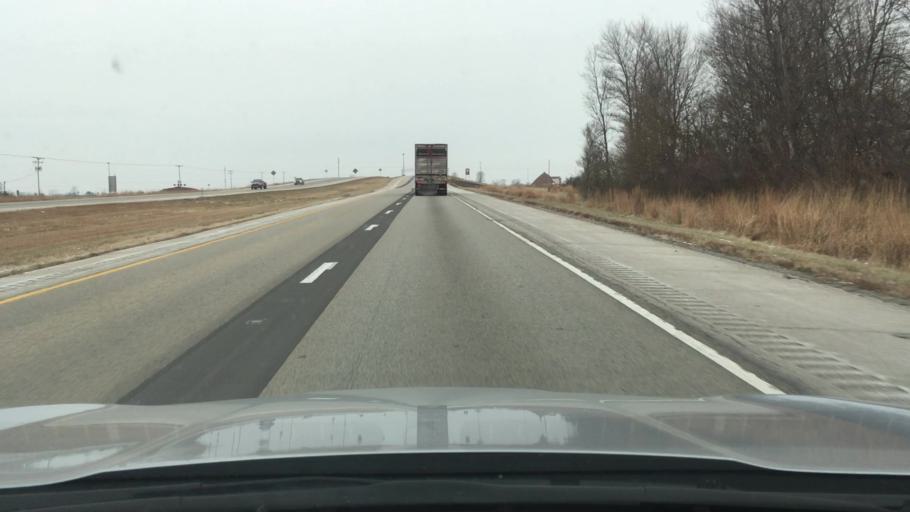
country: US
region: Illinois
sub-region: Sangamon County
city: Divernon
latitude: 39.5842
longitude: -89.6463
